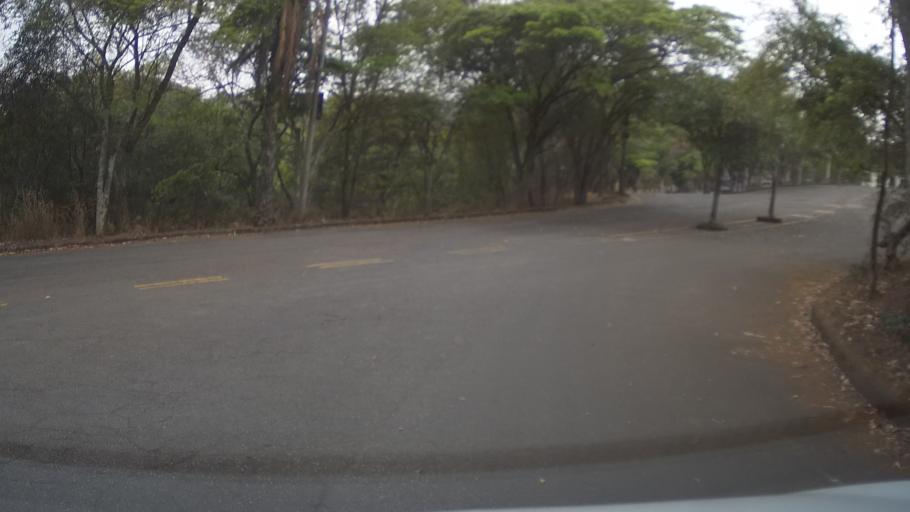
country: BR
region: Minas Gerais
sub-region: Belo Horizonte
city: Belo Horizonte
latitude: -19.9523
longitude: -43.9066
